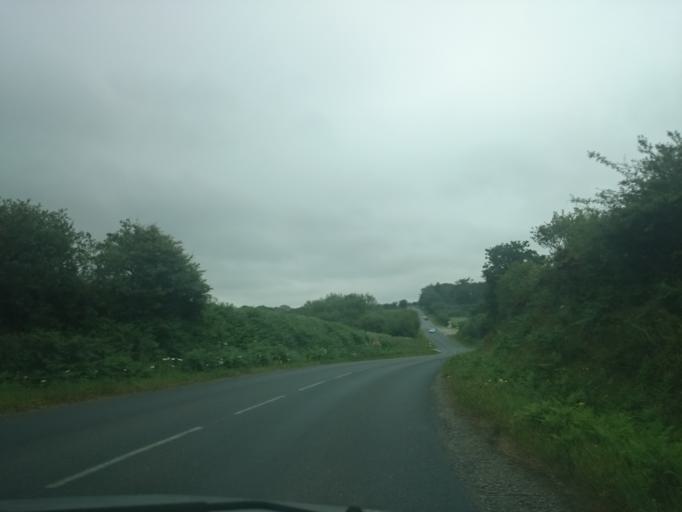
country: FR
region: Brittany
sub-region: Departement du Finistere
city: Saint-Pabu
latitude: 48.5521
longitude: -4.6011
